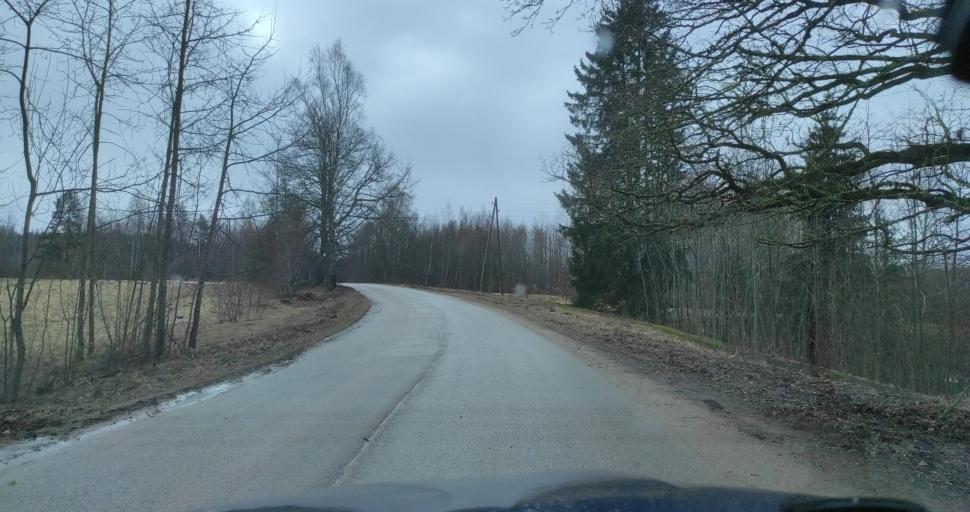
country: LV
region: Tukuma Rajons
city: Tukums
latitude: 57.0895
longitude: 23.0896
